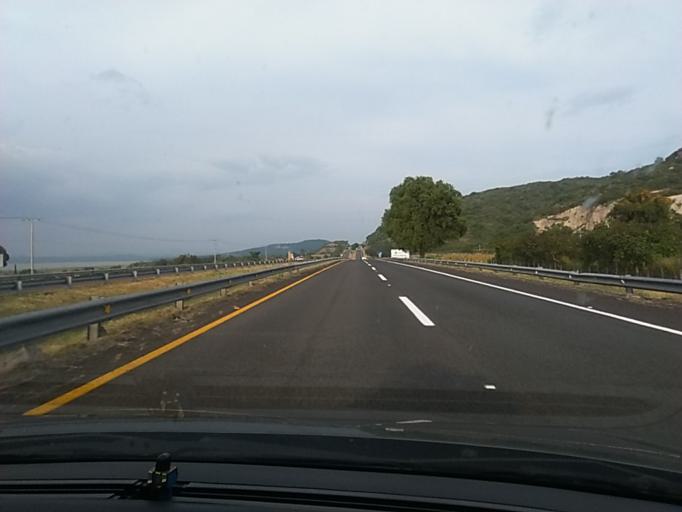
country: MX
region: Michoacan
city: Copandaro de Galeana
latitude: 19.8837
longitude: -101.1942
